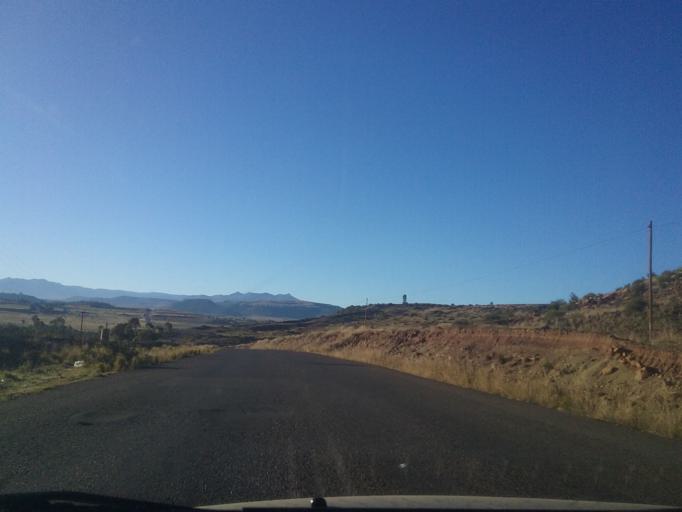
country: LS
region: Quthing
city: Quthing
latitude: -30.3699
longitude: 27.5548
